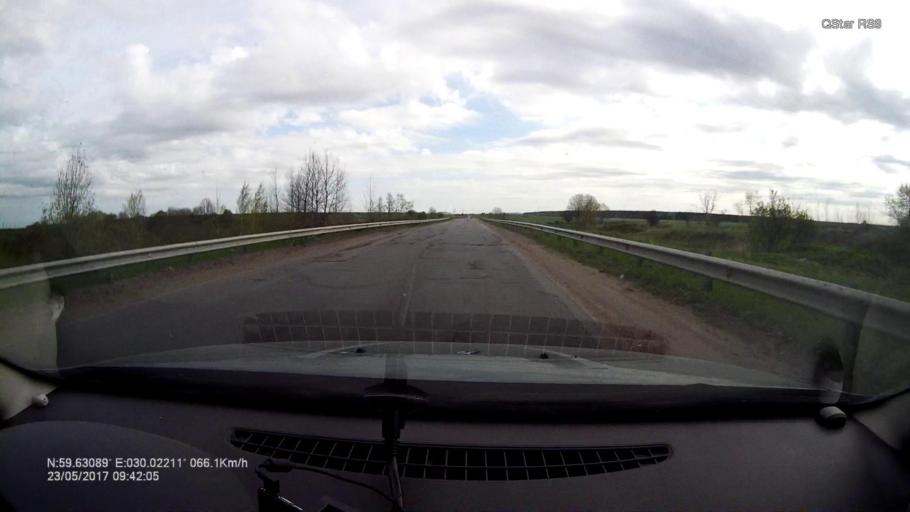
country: RU
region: Leningrad
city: Mariyenburg
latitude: 59.6311
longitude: 30.0224
